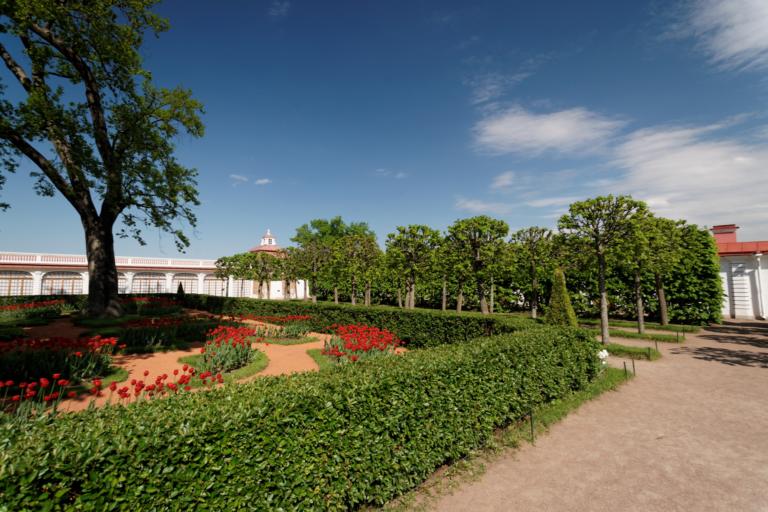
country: RU
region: St.-Petersburg
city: Peterhof
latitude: 59.8868
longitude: 29.9192
